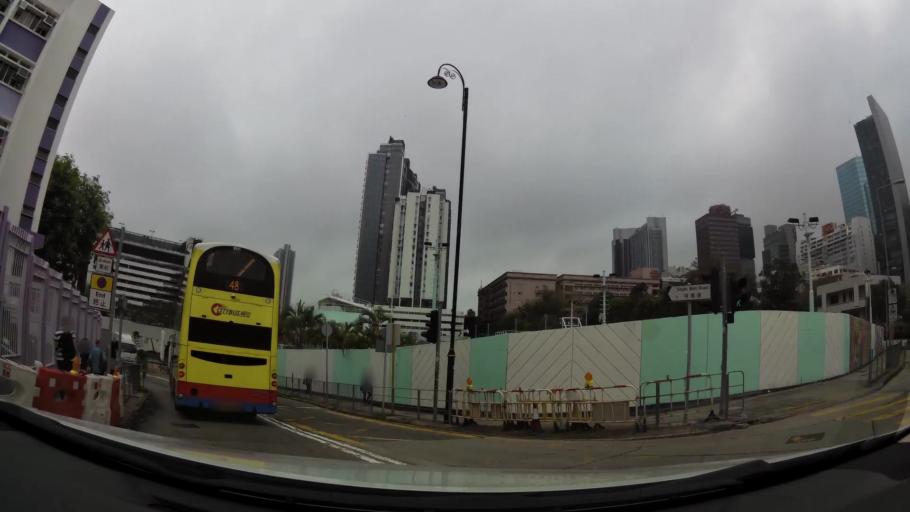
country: HK
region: Wanchai
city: Wan Chai
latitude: 22.2459
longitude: 114.1665
